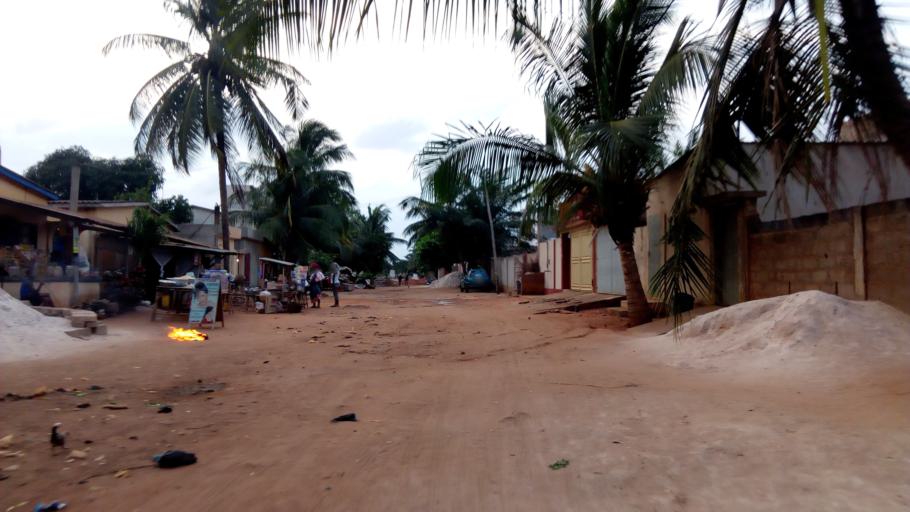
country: TG
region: Maritime
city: Lome
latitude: 6.2297
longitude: 1.1862
